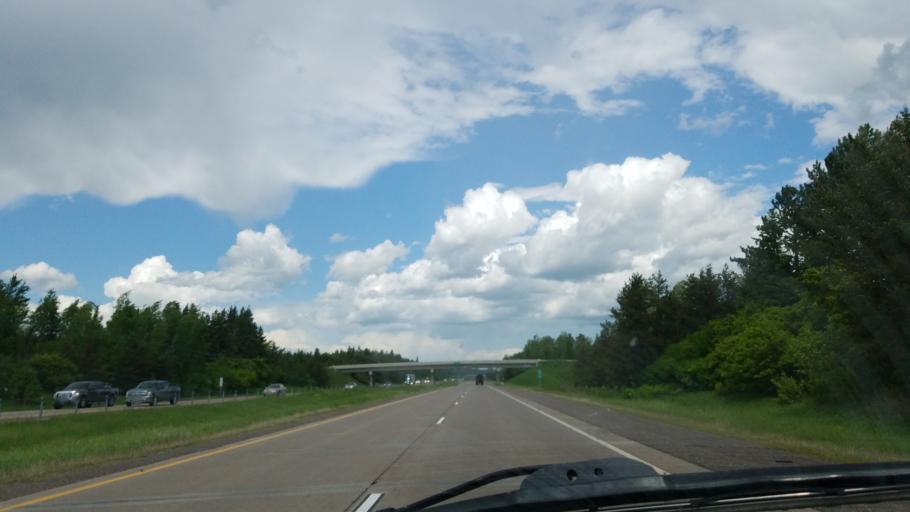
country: US
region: Minnesota
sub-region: Carlton County
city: Moose Lake
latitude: 46.4886
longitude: -92.7018
